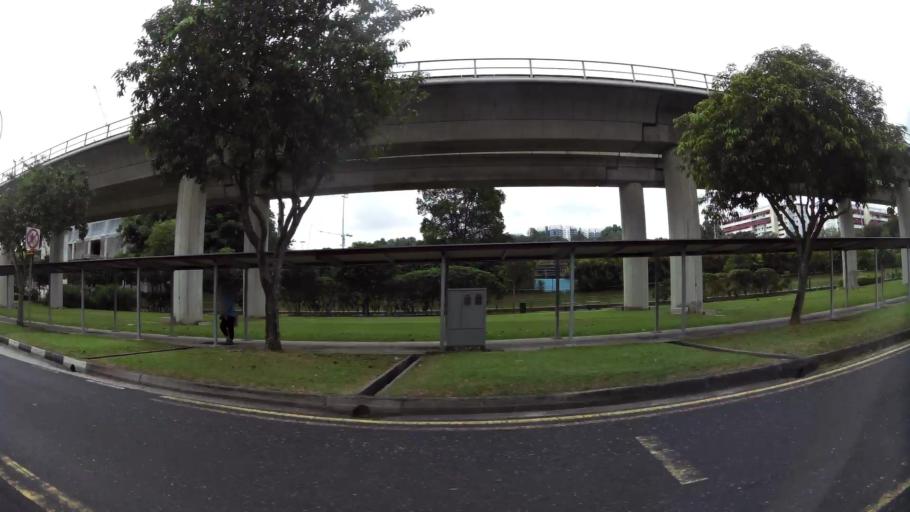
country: MY
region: Johor
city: Johor Bahru
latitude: 1.4335
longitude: 103.7813
